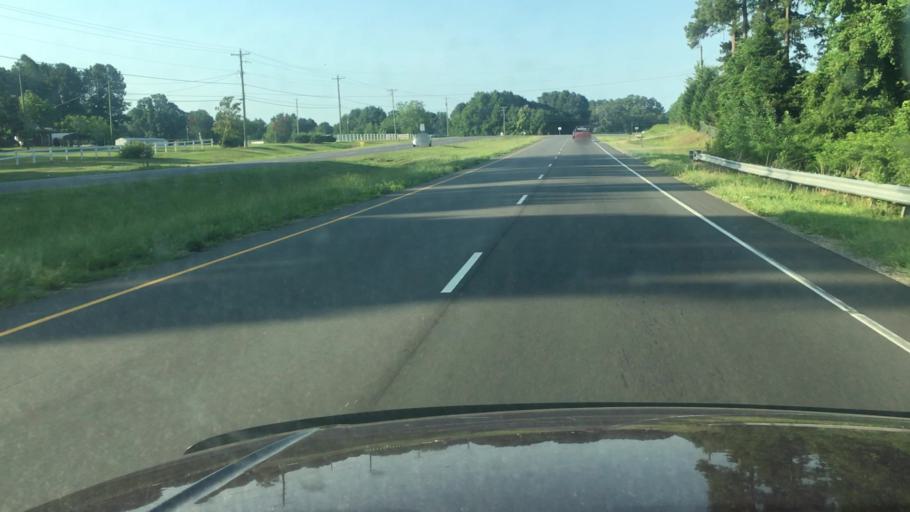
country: US
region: North Carolina
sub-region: Cumberland County
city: Hope Mills
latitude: 34.9391
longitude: -78.8475
